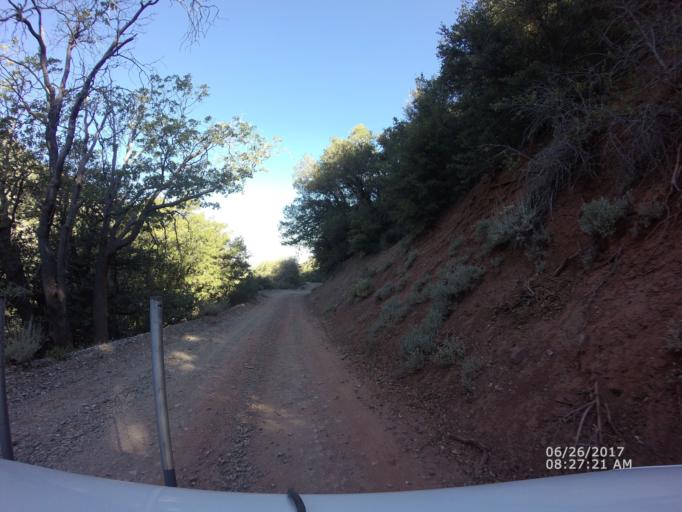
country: US
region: California
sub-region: San Bernardino County
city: Wrightwood
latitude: 34.3748
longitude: -117.7533
